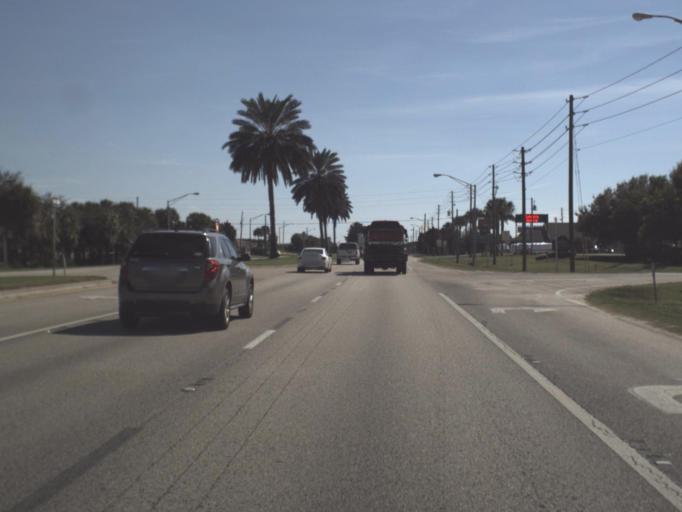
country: US
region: Florida
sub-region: Highlands County
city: Lake Placid
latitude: 27.2958
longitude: -81.3586
